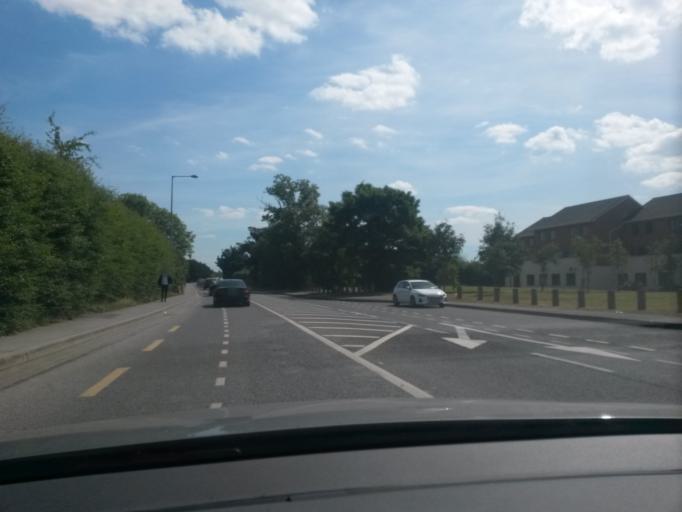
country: IE
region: Leinster
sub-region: Kildare
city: Sallins
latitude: 53.2446
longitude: -6.6660
